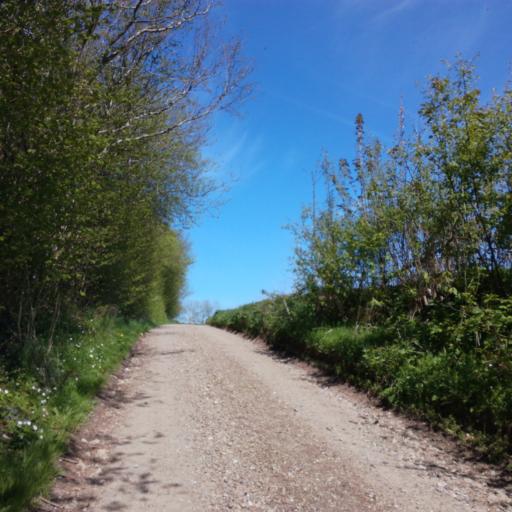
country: DK
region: South Denmark
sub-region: Vejle Kommune
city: Borkop
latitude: 55.6123
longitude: 9.6853
